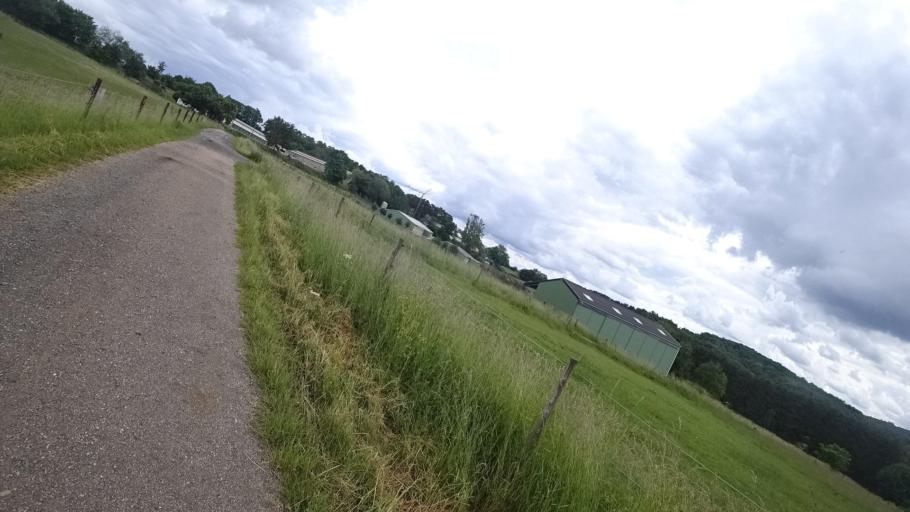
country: DE
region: Rheinland-Pfalz
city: Kalenborn
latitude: 50.5444
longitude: 6.9994
